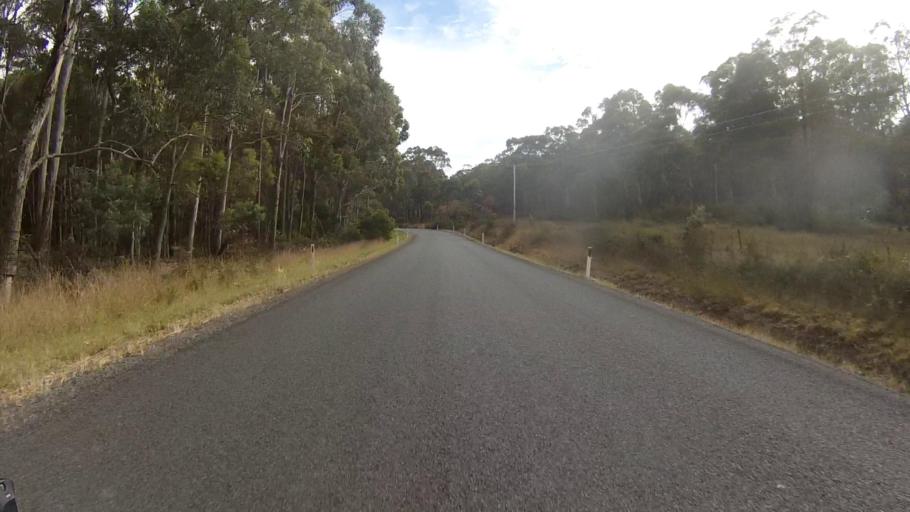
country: AU
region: Tasmania
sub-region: Sorell
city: Sorell
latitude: -42.8152
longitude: 147.7918
